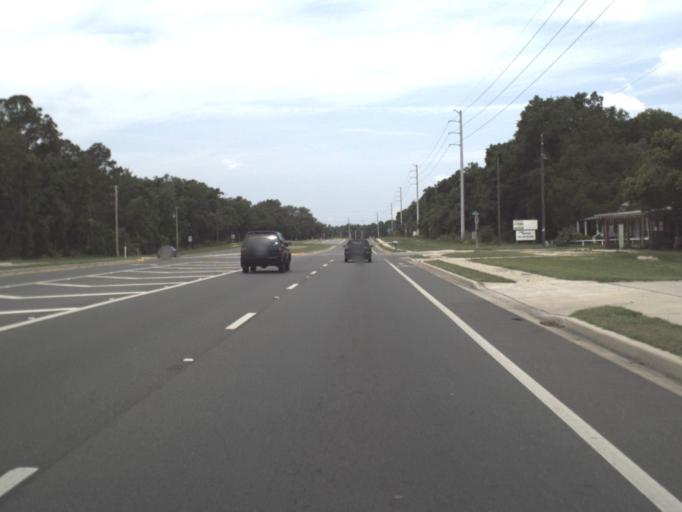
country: US
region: Florida
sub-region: Putnam County
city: Interlachen
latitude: 29.6281
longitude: -81.8677
